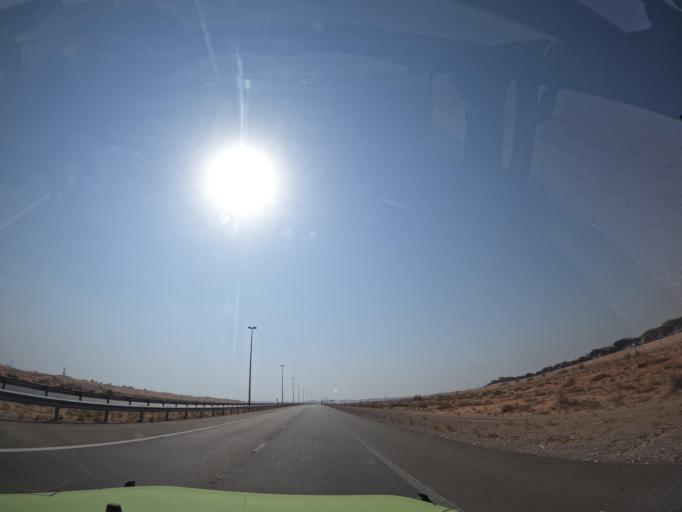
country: OM
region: Al Buraimi
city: Al Buraymi
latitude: 24.4002
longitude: 55.7146
